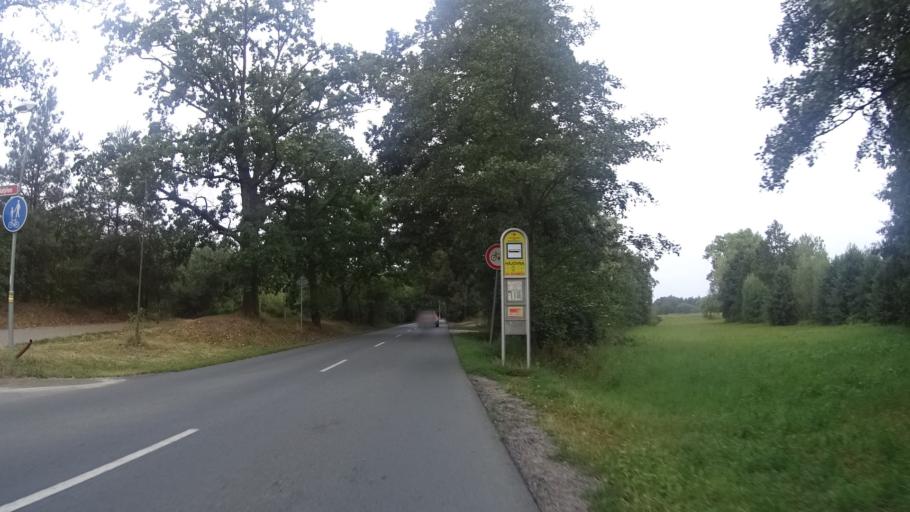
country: CZ
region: Kralovehradecky
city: Cernilov
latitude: 50.2072
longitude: 15.8969
